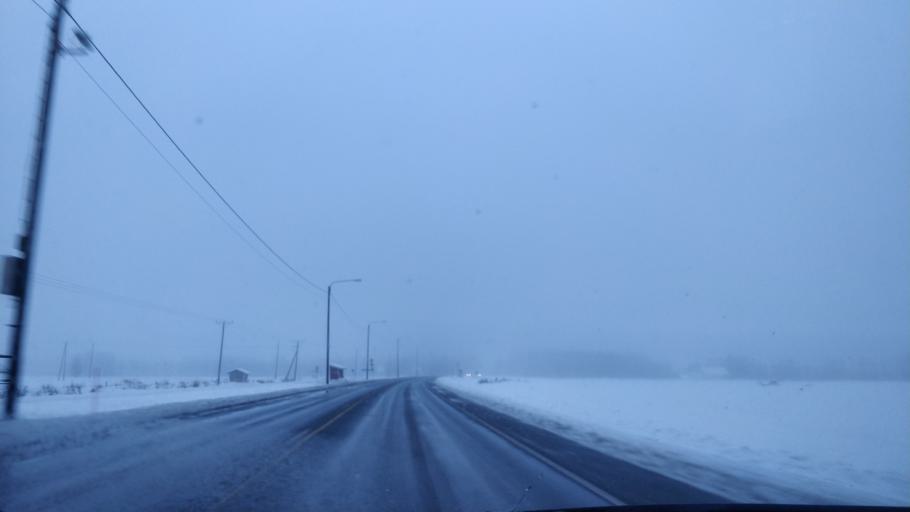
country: FI
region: Lapland
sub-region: Kemi-Tornio
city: Tervola
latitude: 66.1520
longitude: 24.9884
